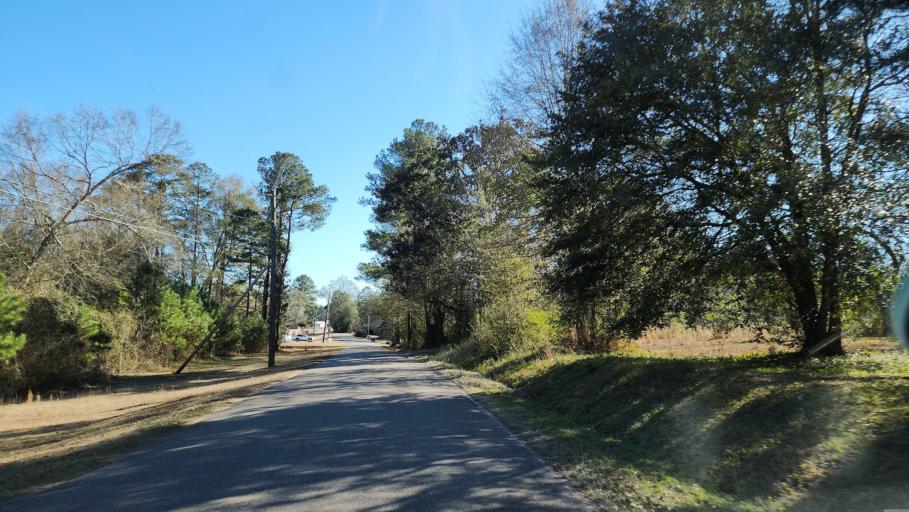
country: US
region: Mississippi
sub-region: Jones County
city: Laurel
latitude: 31.7058
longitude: -89.0925
